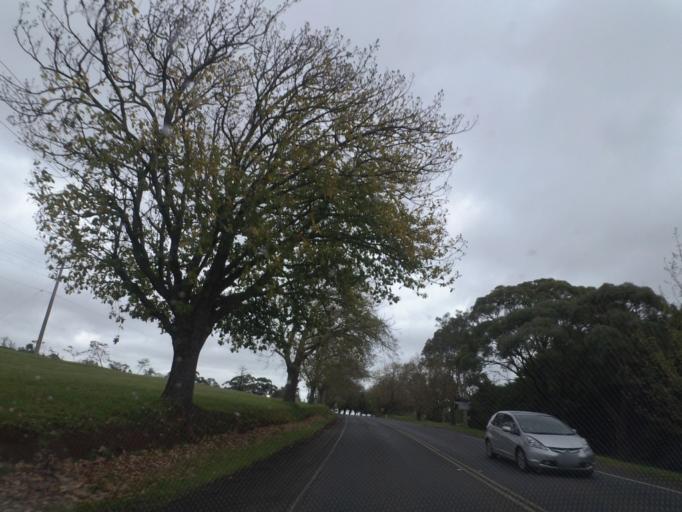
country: AU
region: Victoria
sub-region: Hume
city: Sunbury
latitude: -37.3428
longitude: 144.5310
